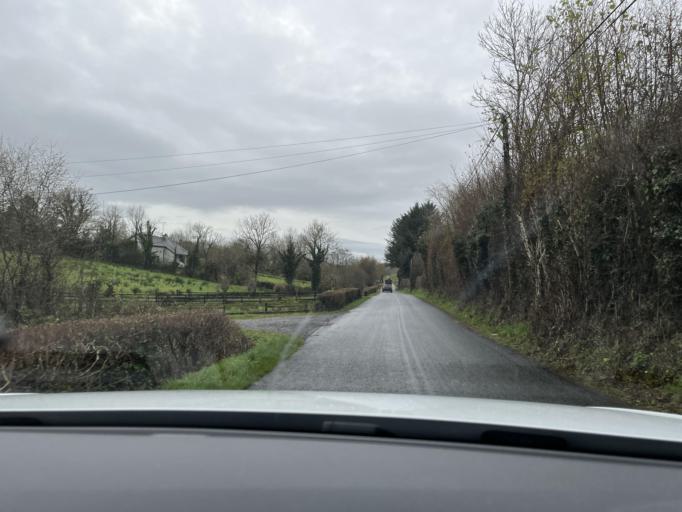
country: IE
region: Connaught
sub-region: County Leitrim
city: Manorhamilton
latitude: 54.2439
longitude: -8.2613
